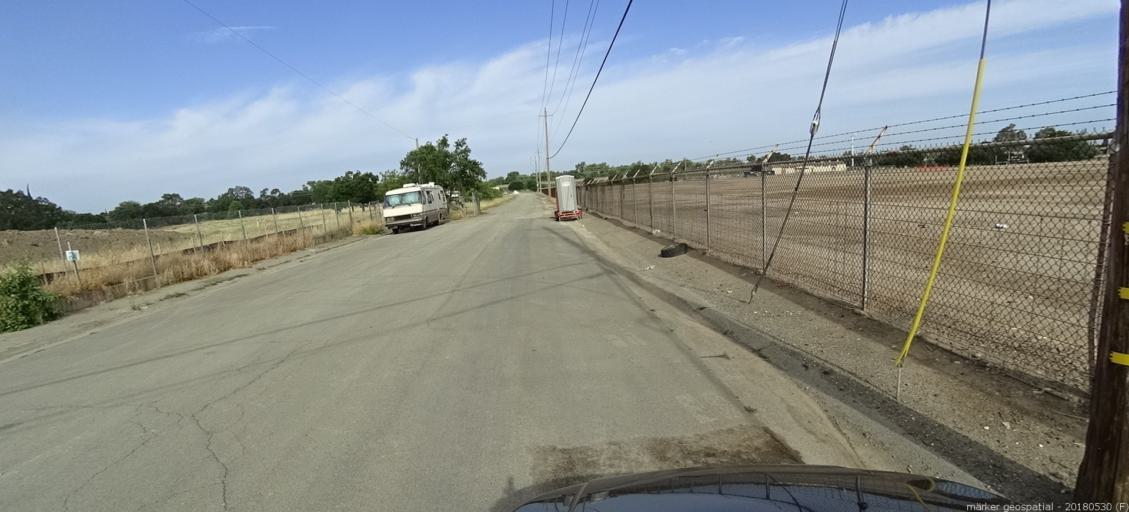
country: US
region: California
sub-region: Sacramento County
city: Sacramento
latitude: 38.6151
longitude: -121.4624
